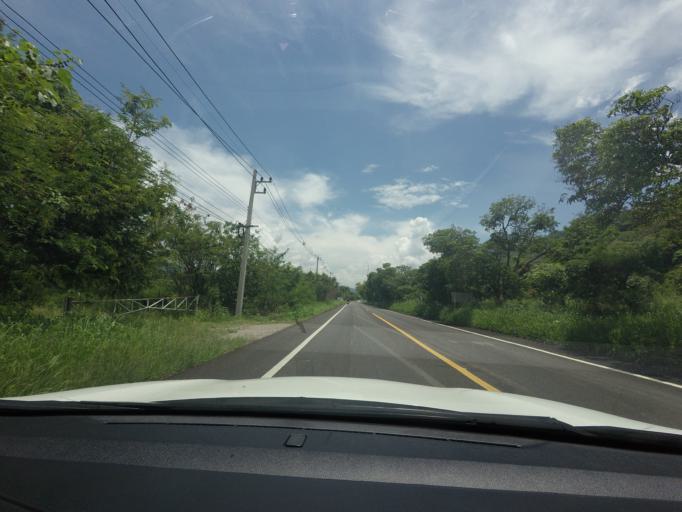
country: TH
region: Sara Buri
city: Muak Lek
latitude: 14.5763
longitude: 101.2729
